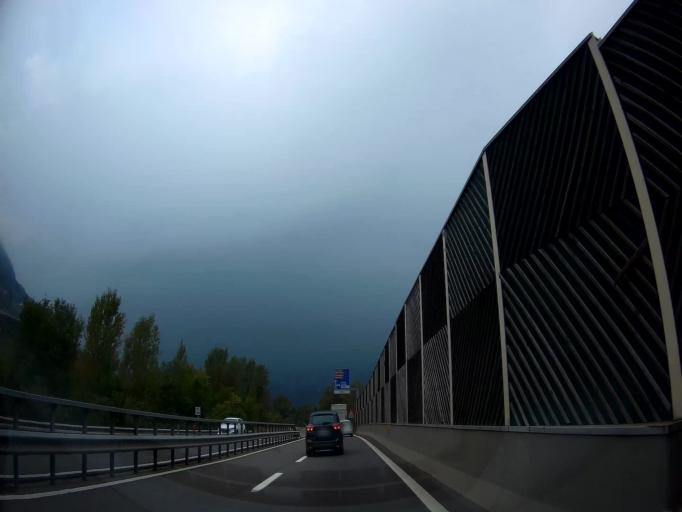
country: IT
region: Trentino-Alto Adige
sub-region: Bolzano
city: Marlengo
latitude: 46.6635
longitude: 11.1447
